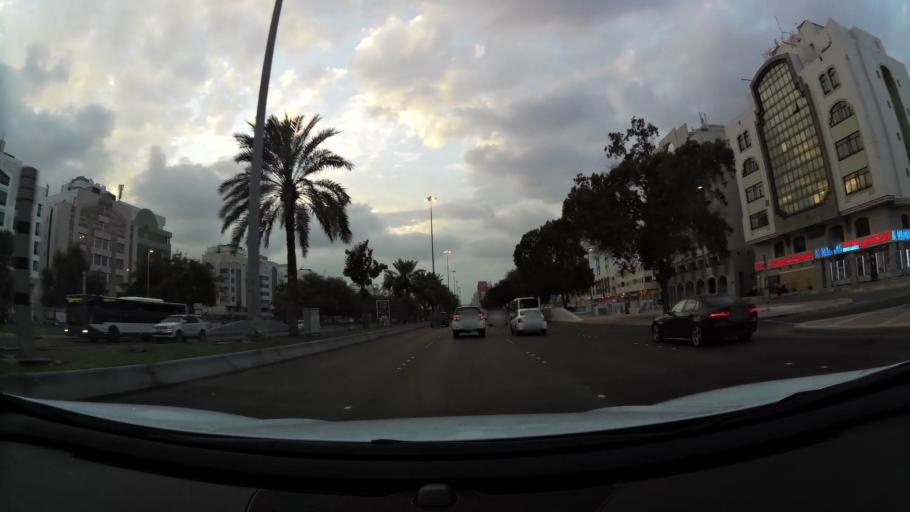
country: AE
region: Abu Dhabi
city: Abu Dhabi
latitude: 24.4524
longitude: 54.3877
